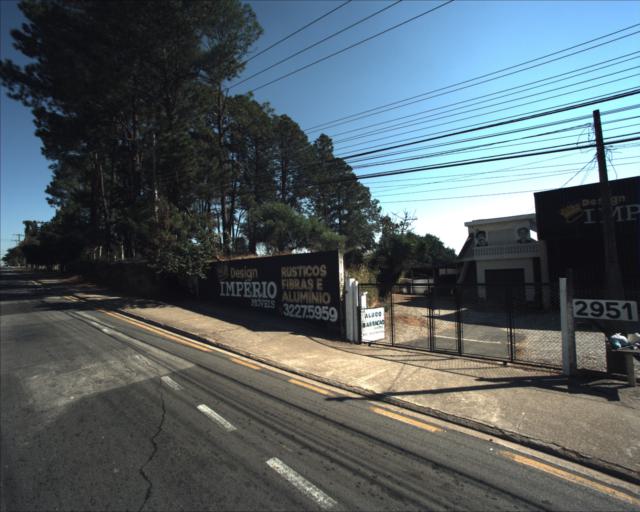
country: BR
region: Sao Paulo
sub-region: Sorocaba
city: Sorocaba
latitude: -23.4890
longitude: -47.4262
